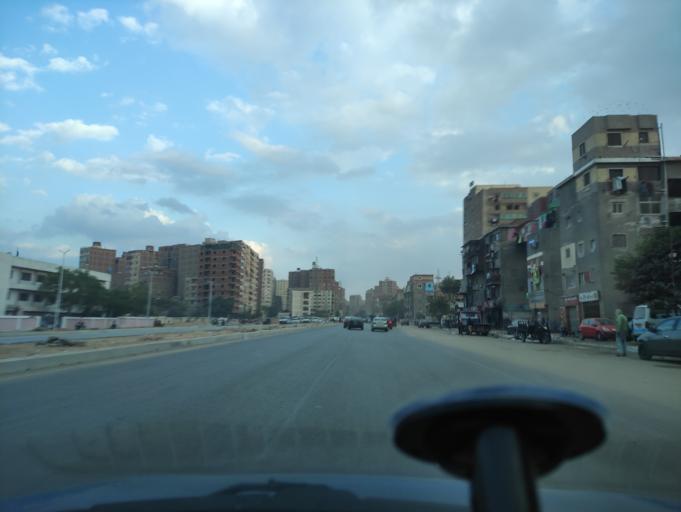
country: EG
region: Muhafazat al Qalyubiyah
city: Al Khankah
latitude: 30.1349
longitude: 31.3548
